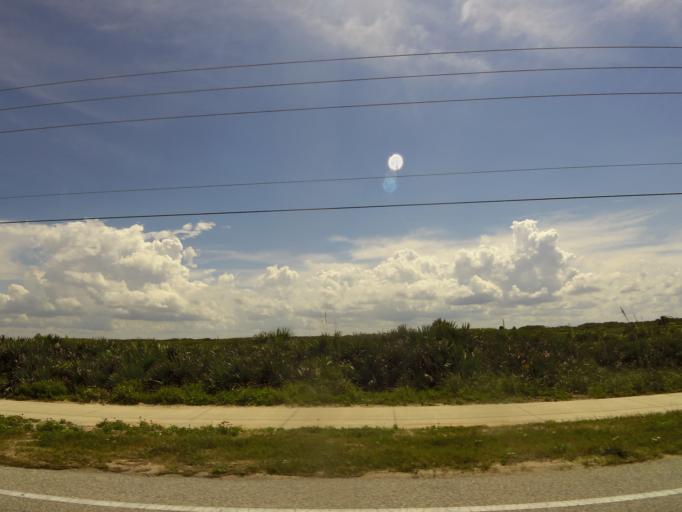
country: US
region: Florida
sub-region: Volusia County
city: Ormond-by-the-Sea
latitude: 29.3961
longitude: -81.0885
